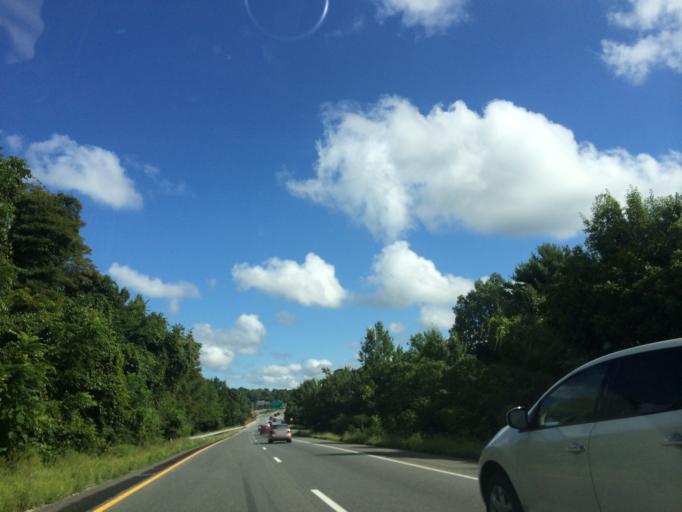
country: US
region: Maryland
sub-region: Howard County
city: Ellicott City
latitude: 39.2939
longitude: -76.8255
